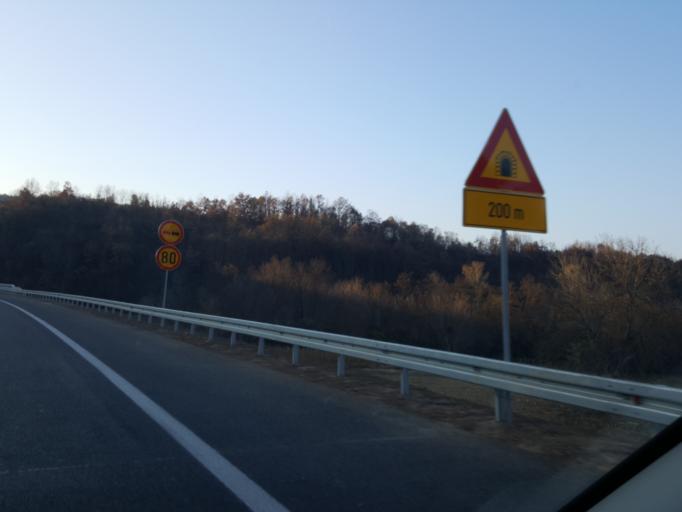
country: RS
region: Central Serbia
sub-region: Pirotski Okrug
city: Pirot
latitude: 43.2172
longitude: 22.5433
